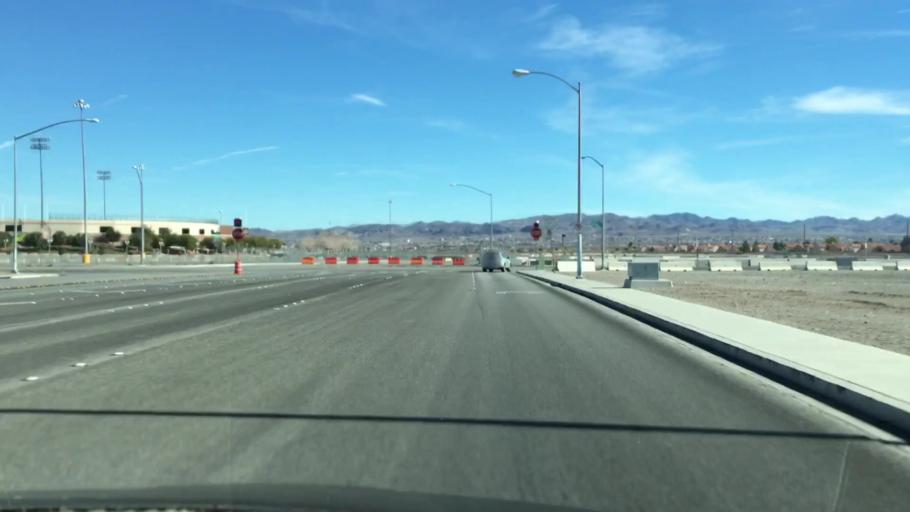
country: US
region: Nevada
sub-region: Clark County
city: Henderson
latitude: 36.0852
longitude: -115.0213
